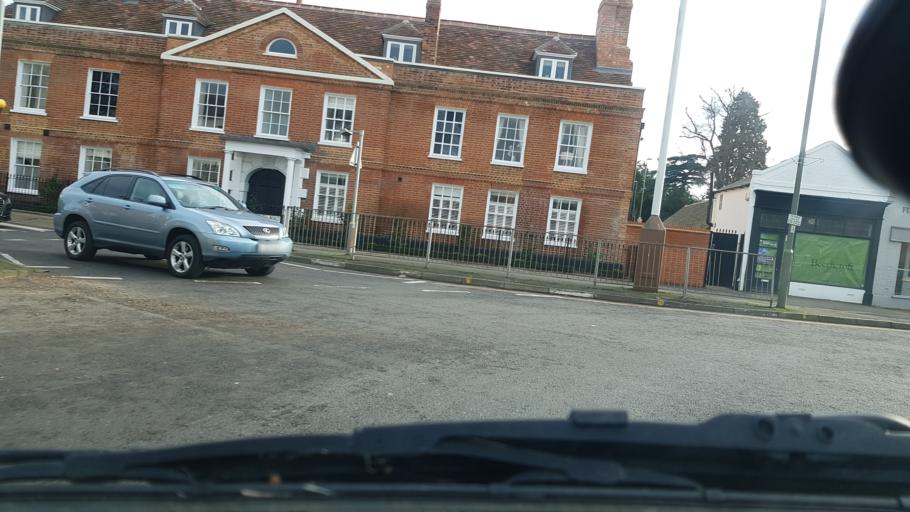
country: GB
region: England
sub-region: Surrey
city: Cobham
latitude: 51.3321
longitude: -0.4179
